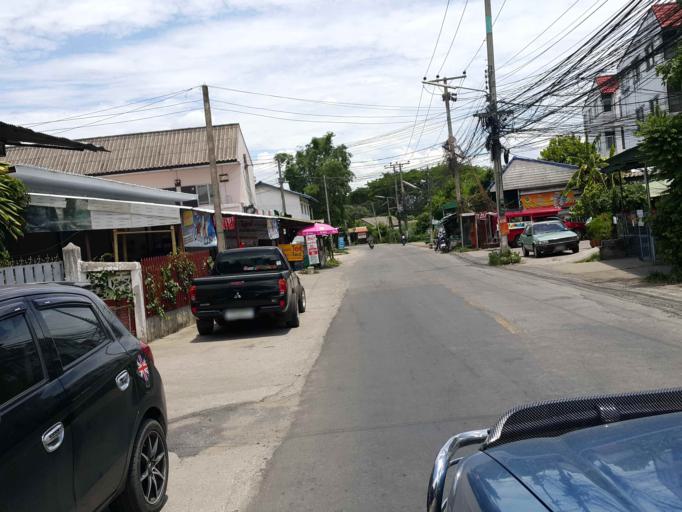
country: TH
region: Chiang Mai
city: Chiang Mai
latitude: 18.7734
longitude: 99.0214
